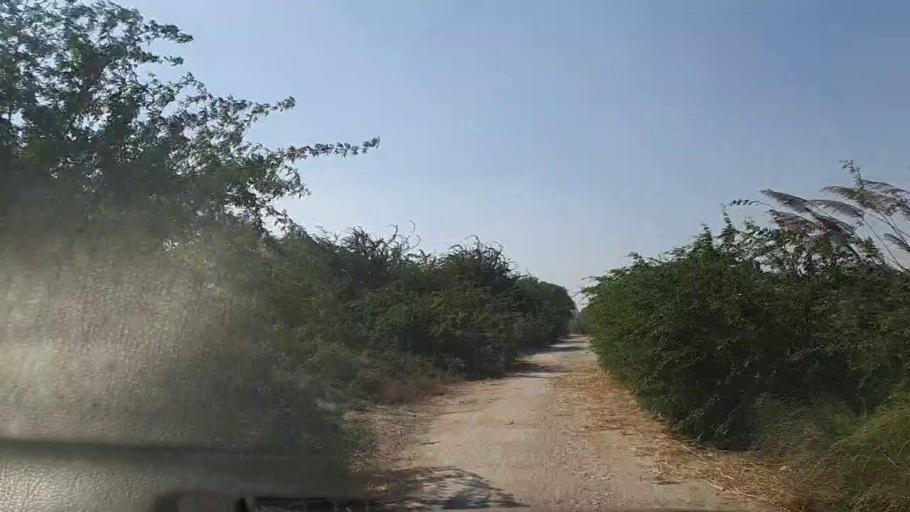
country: PK
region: Sindh
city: Daro Mehar
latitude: 24.8377
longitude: 68.1134
